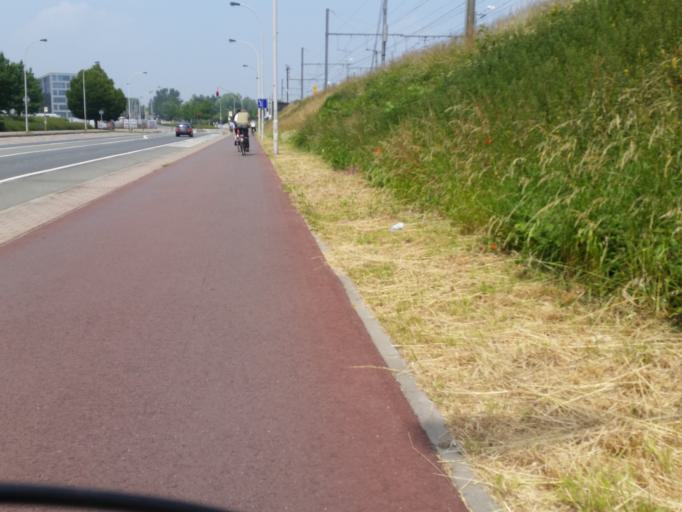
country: BE
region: Flanders
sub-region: Provincie Antwerpen
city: Mortsel
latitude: 51.1916
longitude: 4.4387
